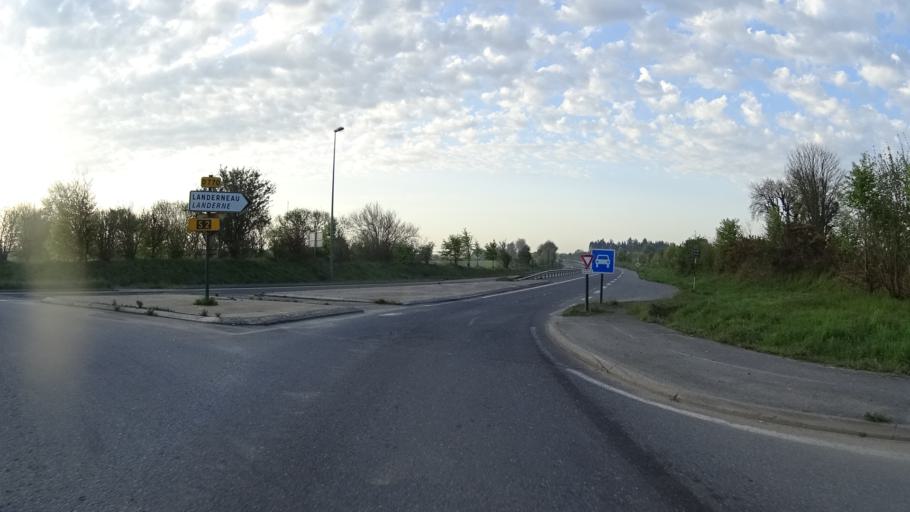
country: FR
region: Brittany
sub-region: Departement du Finistere
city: Plouedern
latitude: 48.4783
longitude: -4.2869
